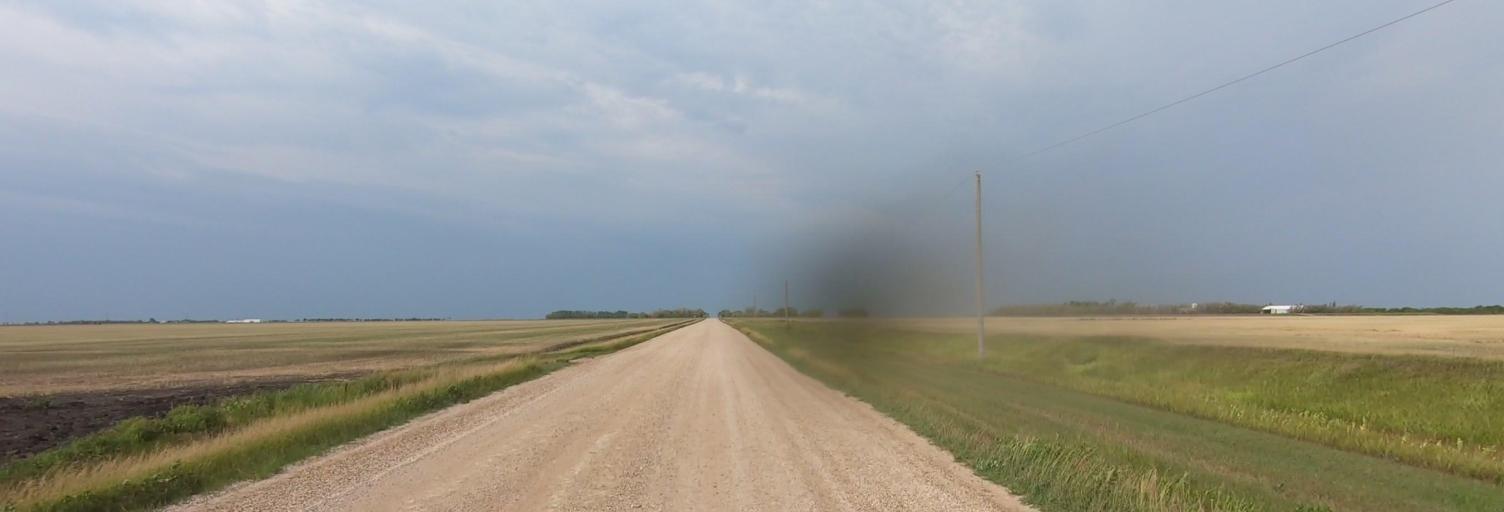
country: CA
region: Manitoba
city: Morris
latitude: 49.5765
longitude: -97.3329
